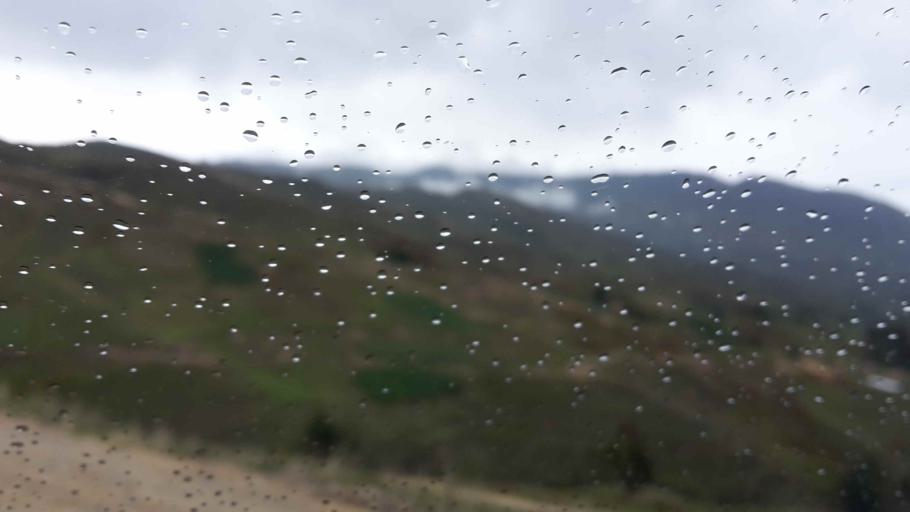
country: BO
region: Cochabamba
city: Cochabamba
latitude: -17.1379
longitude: -66.1064
